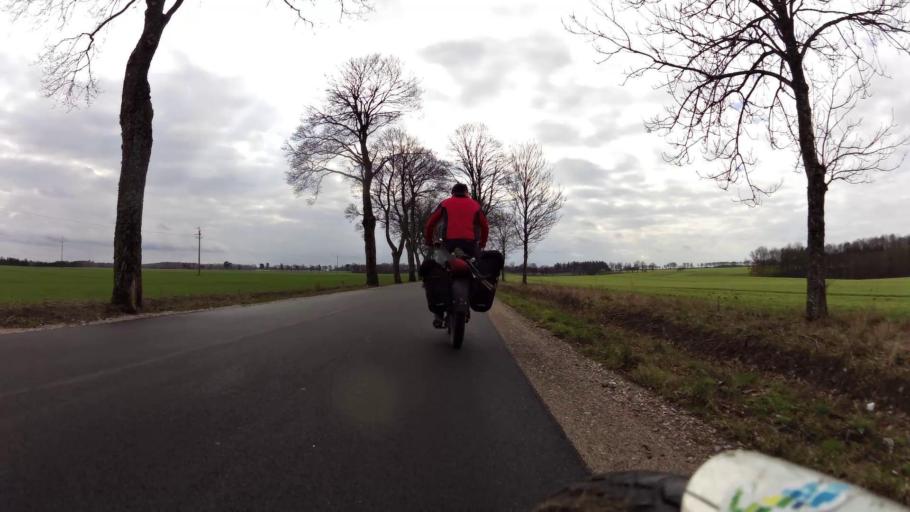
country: PL
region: Pomeranian Voivodeship
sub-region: Powiat bytowski
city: Kolczyglowy
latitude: 54.2320
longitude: 17.2422
